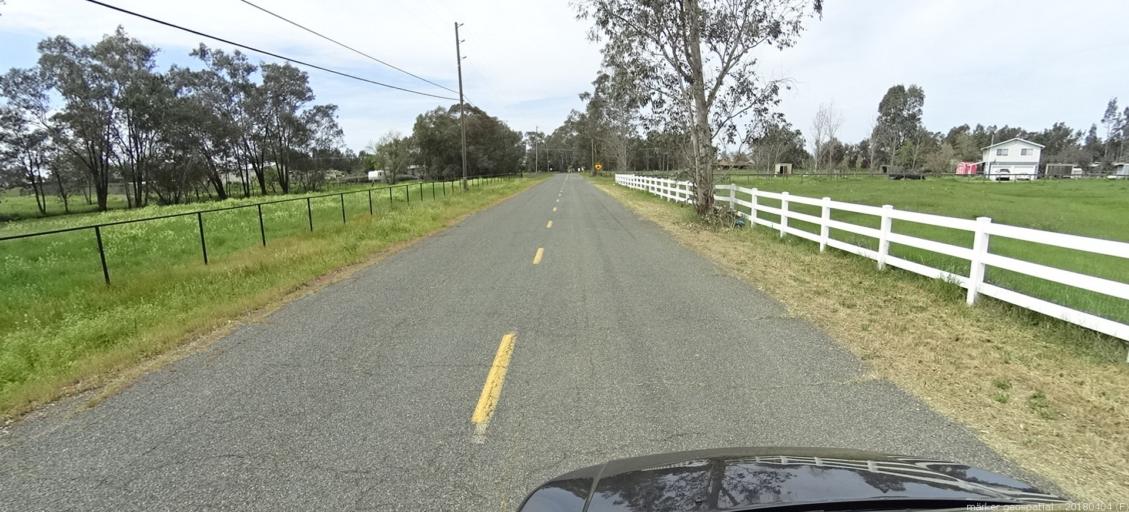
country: US
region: California
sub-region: Sacramento County
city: Clay
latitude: 38.3140
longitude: -121.1681
